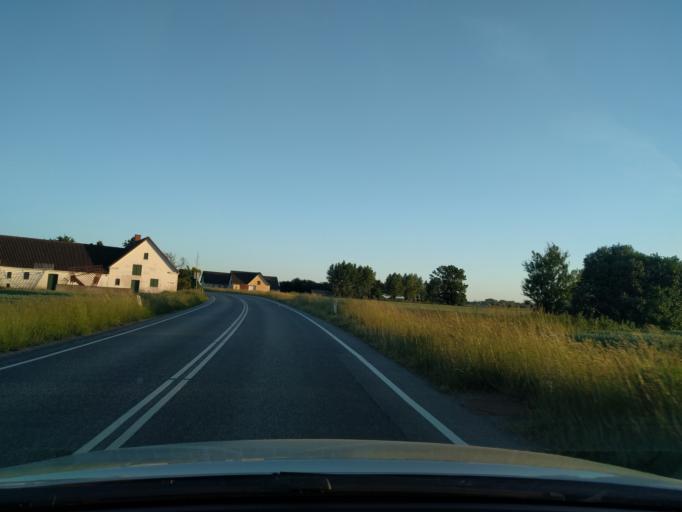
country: DK
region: South Denmark
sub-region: Kerteminde Kommune
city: Munkebo
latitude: 55.4763
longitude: 10.6035
